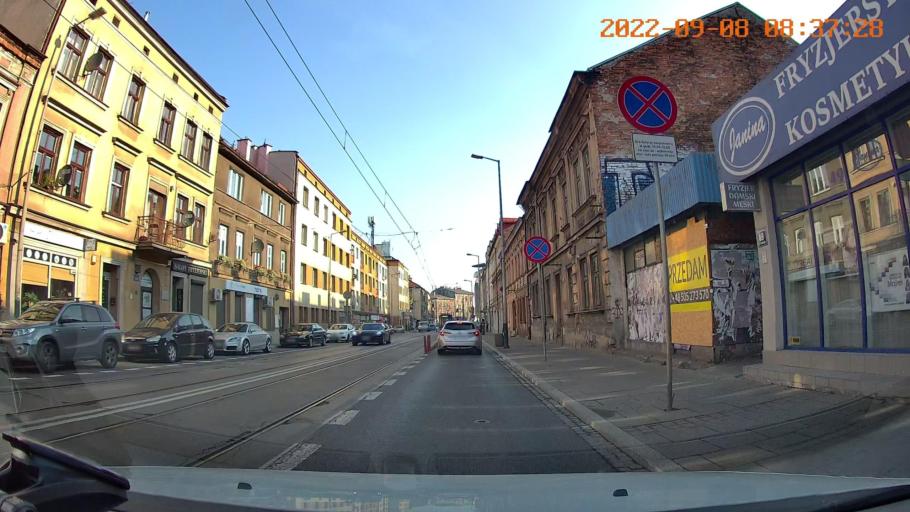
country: PL
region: Lesser Poland Voivodeship
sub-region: Krakow
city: Krakow
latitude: 50.0397
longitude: 19.9423
